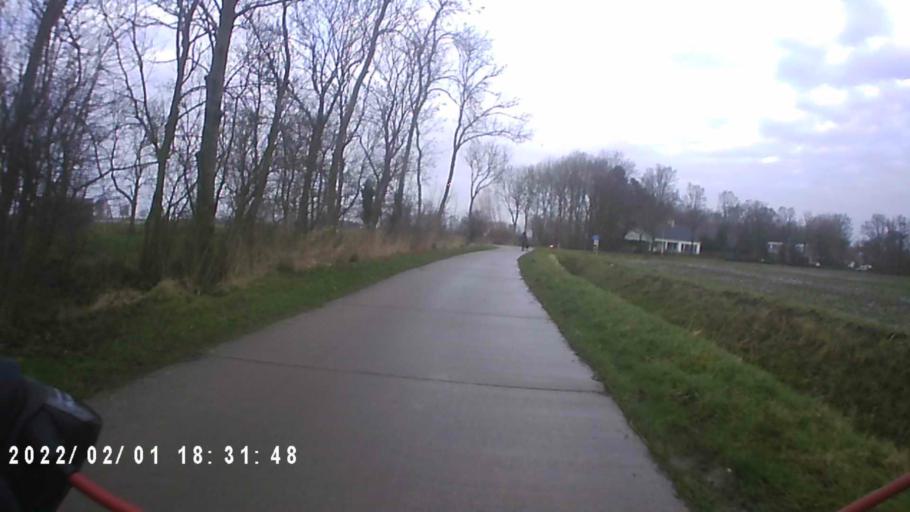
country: NL
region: Groningen
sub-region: Gemeente De Marne
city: Ulrum
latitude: 53.3591
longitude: 6.3208
